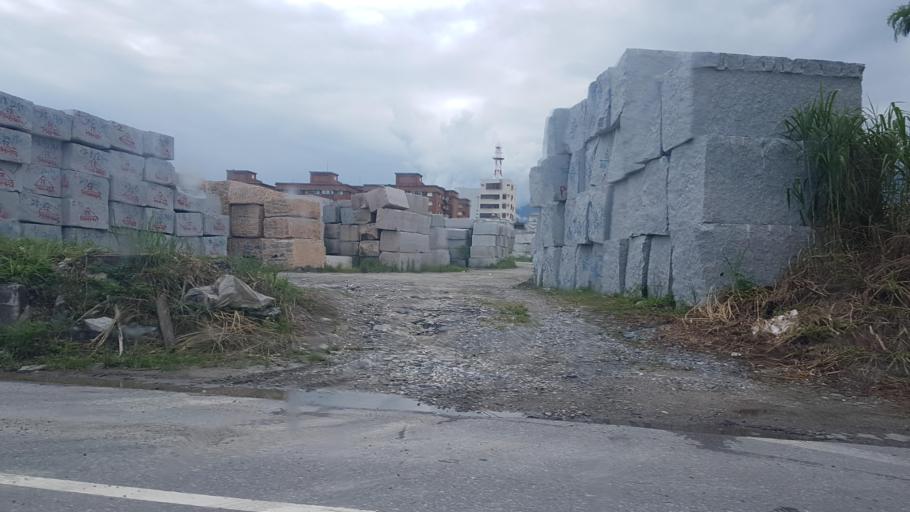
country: TW
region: Taiwan
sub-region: Hualien
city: Hualian
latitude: 24.0022
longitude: 121.6344
